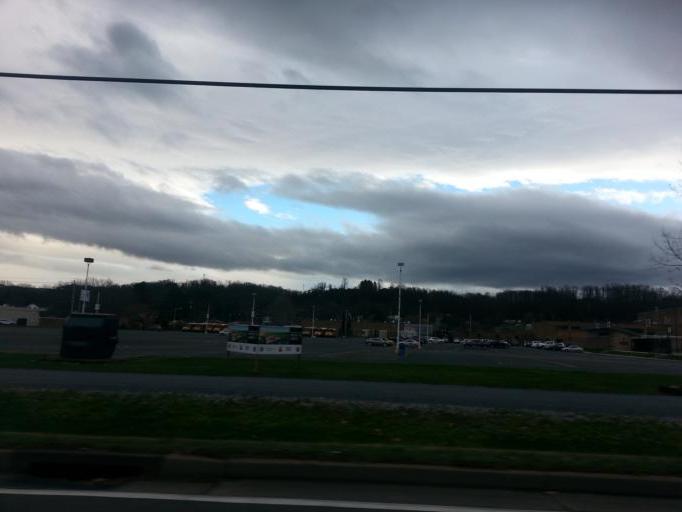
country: US
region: Tennessee
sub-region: Carter County
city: Elizabethton
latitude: 36.3489
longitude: -82.2400
